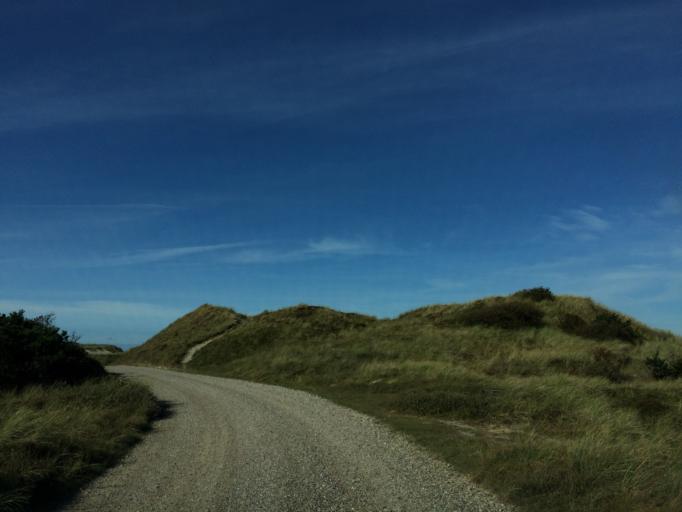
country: DK
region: Central Jutland
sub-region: Holstebro Kommune
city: Ulfborg
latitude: 56.2894
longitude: 8.1321
